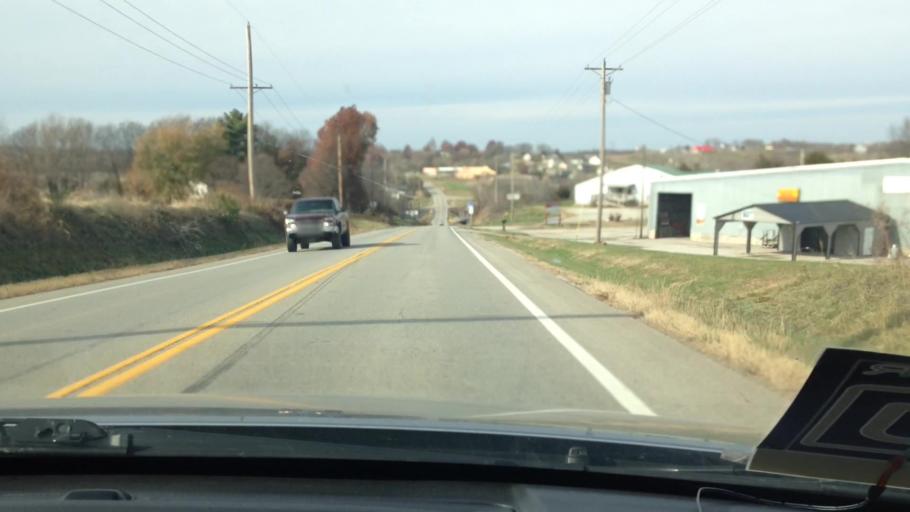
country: US
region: Missouri
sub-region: Platte County
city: Weston
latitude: 39.4158
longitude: -94.8891
